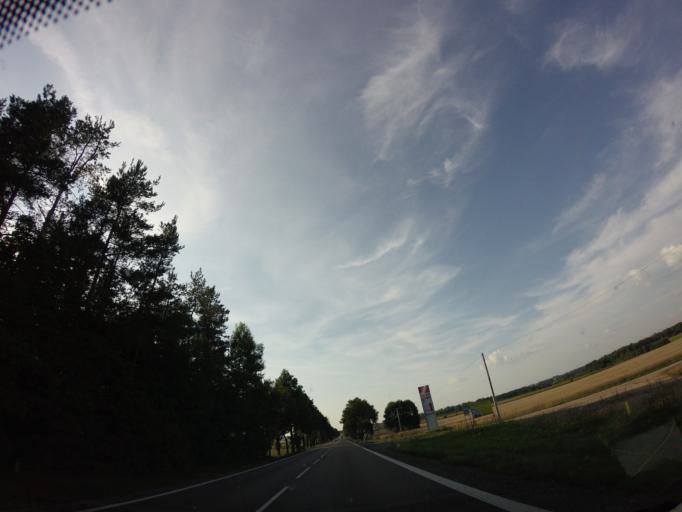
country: PL
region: Podlasie
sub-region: Powiat sokolski
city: Janow
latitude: 53.4295
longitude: 23.1042
